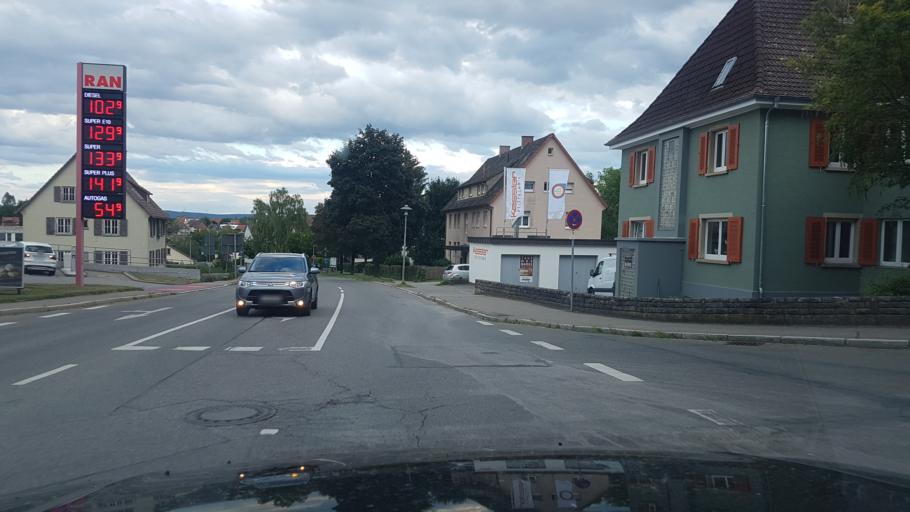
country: DE
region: Baden-Wuerttemberg
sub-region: Freiburg Region
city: Donaueschingen
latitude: 47.9567
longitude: 8.4841
